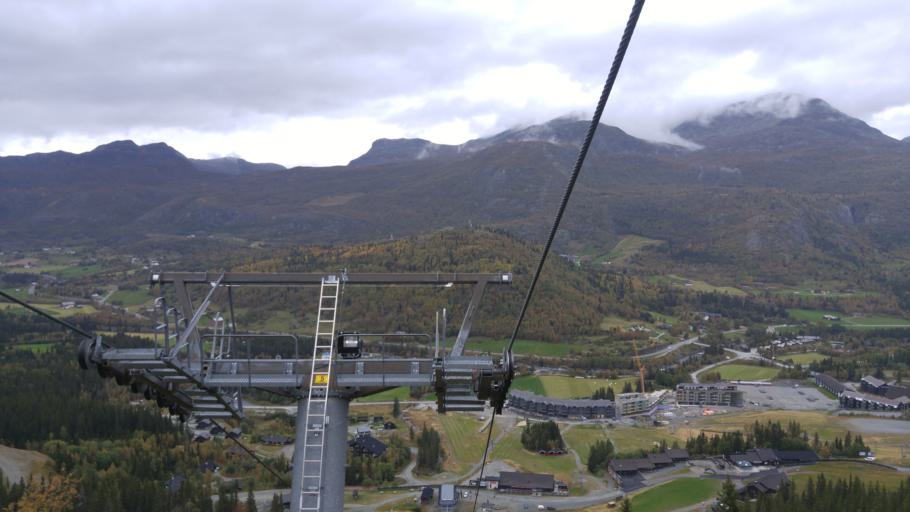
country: NO
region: Buskerud
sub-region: Hemsedal
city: Hemsedal
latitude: 60.8568
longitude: 8.5129
